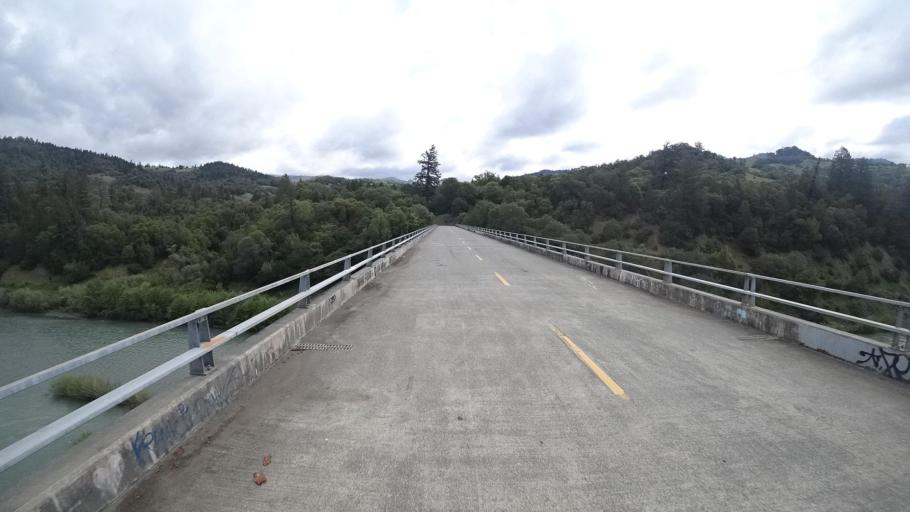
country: US
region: California
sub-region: Humboldt County
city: Redway
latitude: 40.1733
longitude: -123.6043
